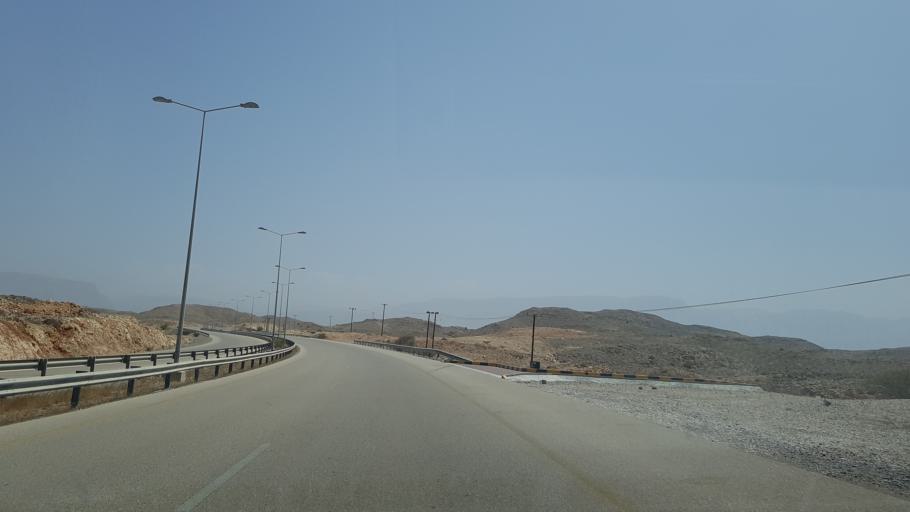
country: OM
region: Muhafazat Masqat
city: Muscat
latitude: 23.1645
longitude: 58.9748
